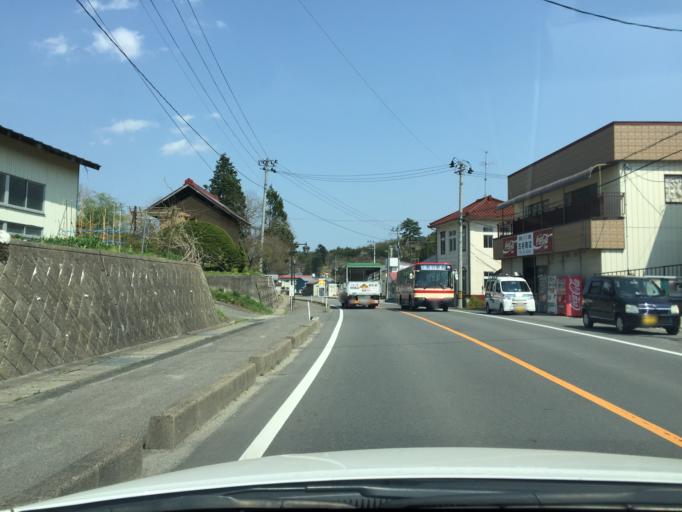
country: JP
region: Fukushima
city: Funehikimachi-funehiki
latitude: 37.4581
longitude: 140.7341
